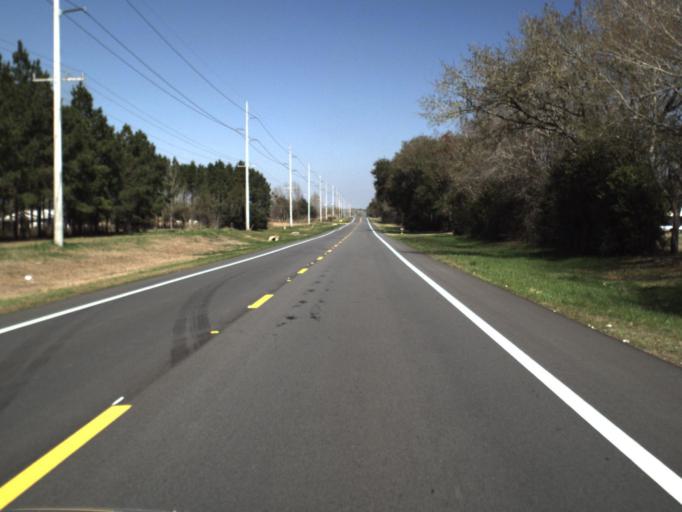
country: US
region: Florida
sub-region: Jackson County
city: Sneads
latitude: 30.7632
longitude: -85.0193
